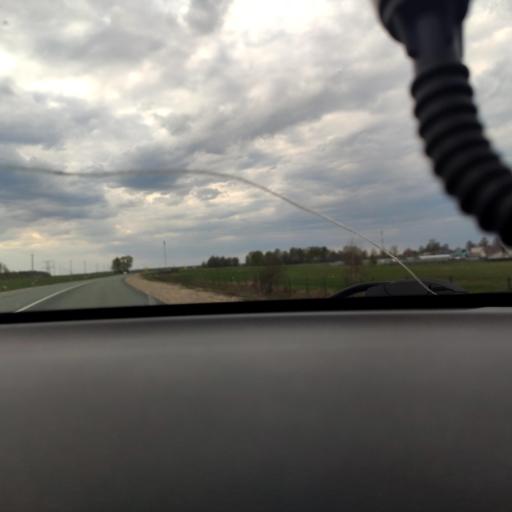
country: RU
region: Mariy-El
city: Krasnogorskiy
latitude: 56.1888
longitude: 48.2442
